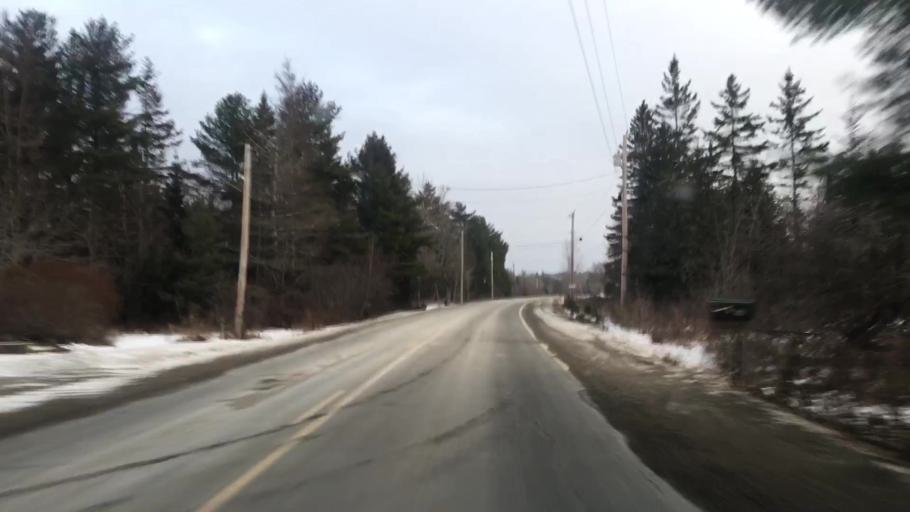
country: US
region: Maine
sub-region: Hancock County
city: Franklin
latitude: 44.6899
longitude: -68.3487
